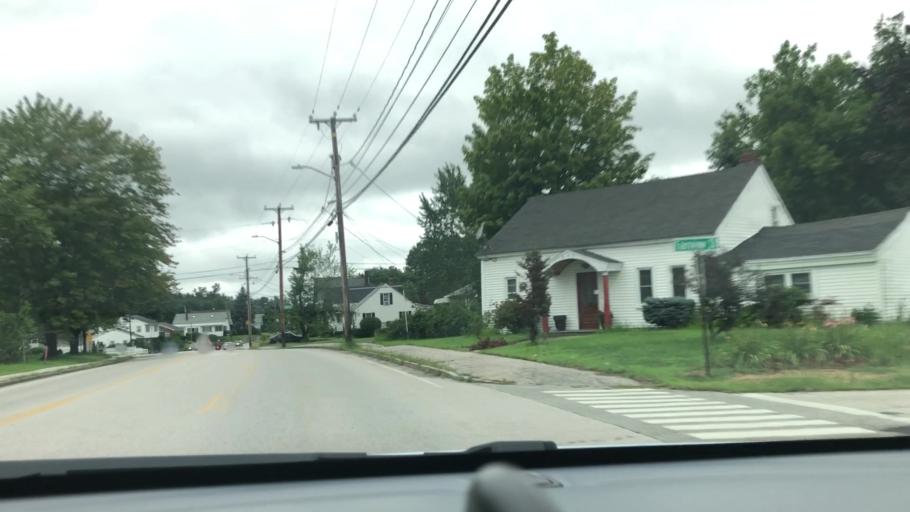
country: US
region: New Hampshire
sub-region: Hillsborough County
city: Pinardville
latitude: 42.9955
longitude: -71.5092
